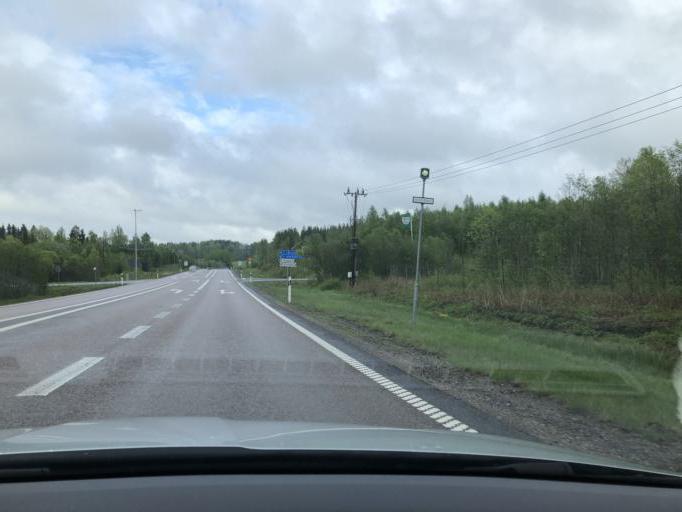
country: SE
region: Vaesternorrland
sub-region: OErnskoeldsviks Kommun
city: Ornskoldsvik
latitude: 63.3099
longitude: 18.9336
